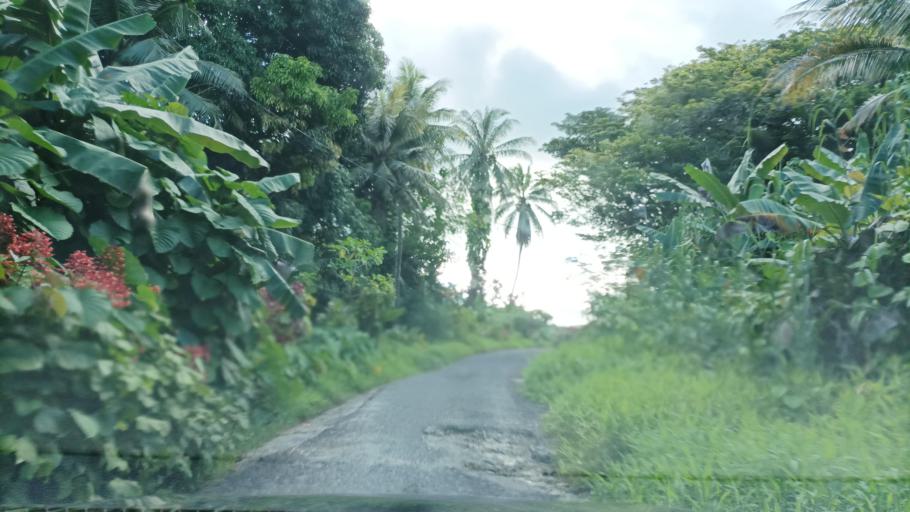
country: FM
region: Pohnpei
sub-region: Madolenihm Municipality
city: Madolenihm Municipality Government
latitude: 6.8426
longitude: 158.3094
